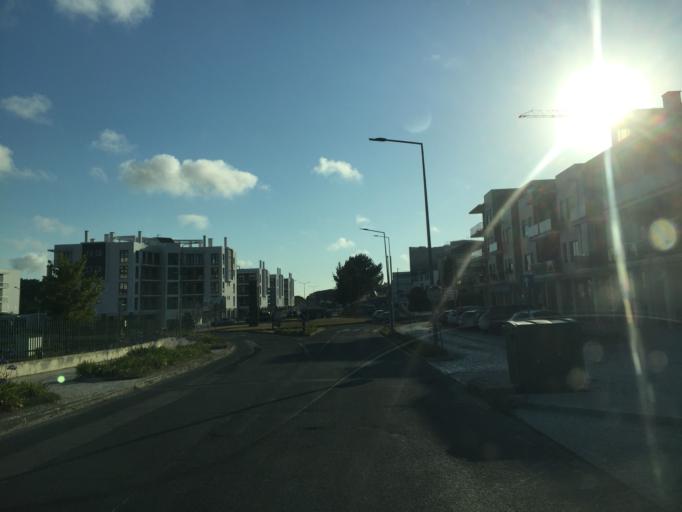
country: PT
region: Leiria
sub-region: Caldas da Rainha
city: Caldas da Rainha
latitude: 39.3980
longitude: -9.1327
